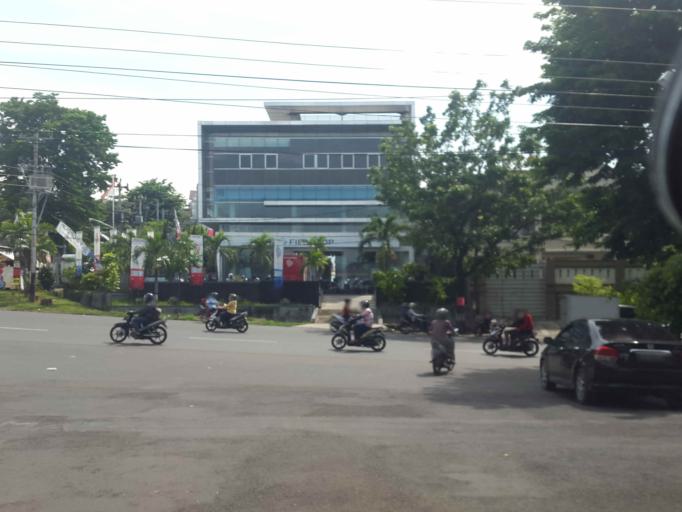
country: ID
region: Central Java
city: Semarang
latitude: -6.9887
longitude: 110.3942
